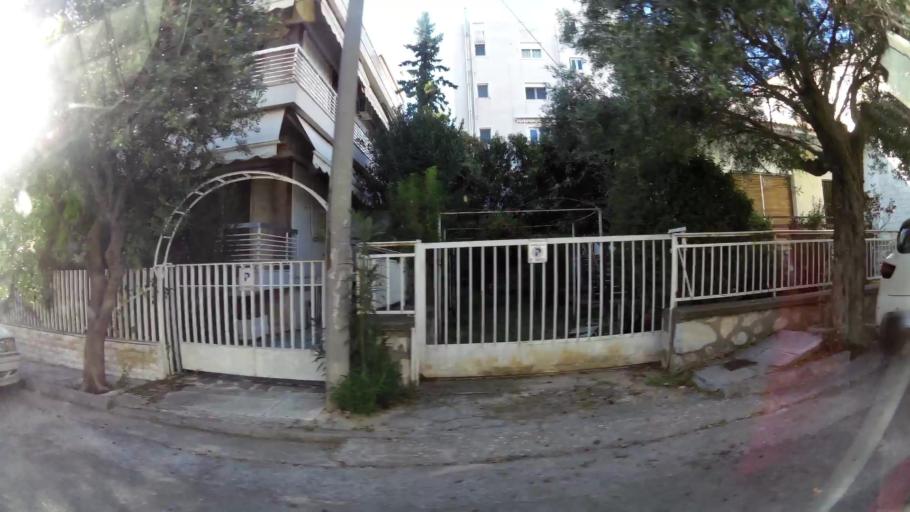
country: GR
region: Attica
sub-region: Nomarchia Anatolikis Attikis
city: Pallini
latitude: 38.0006
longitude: 23.8750
